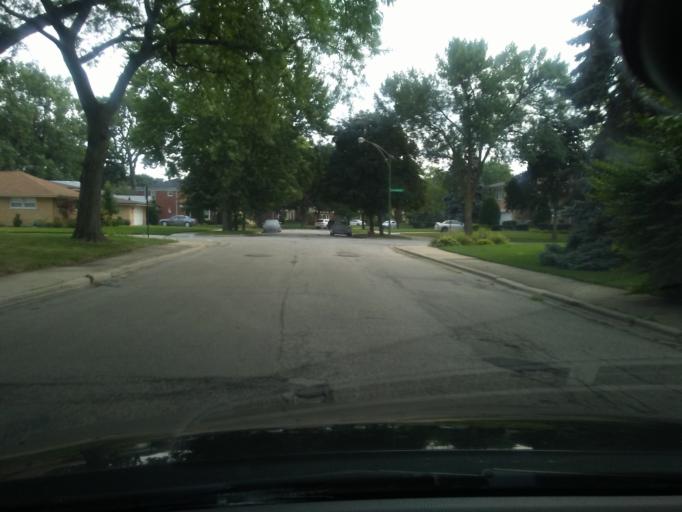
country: US
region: Illinois
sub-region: Cook County
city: Lincolnwood
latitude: 41.9960
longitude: -87.7411
